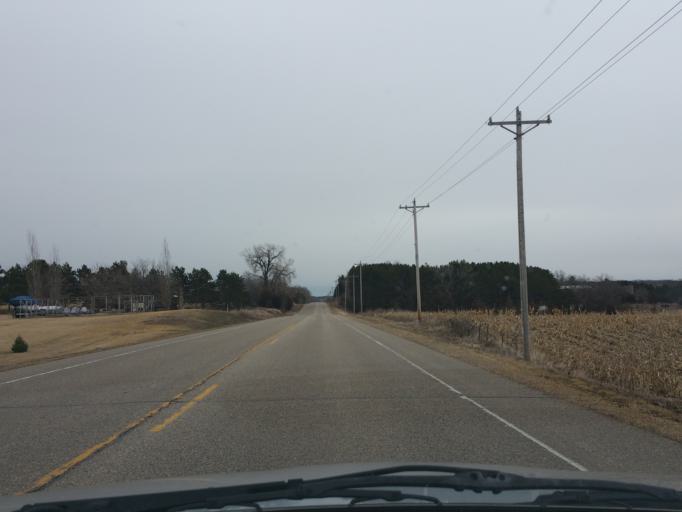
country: US
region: Wisconsin
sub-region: Saint Croix County
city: North Hudson
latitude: 45.0033
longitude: -92.6698
